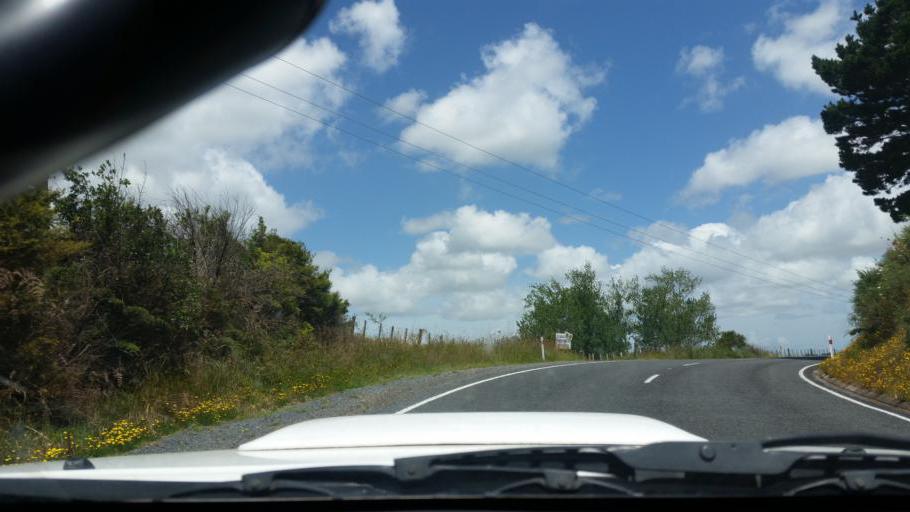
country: NZ
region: Northland
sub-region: Whangarei
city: Ruakaka
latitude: -36.0513
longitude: 174.2761
